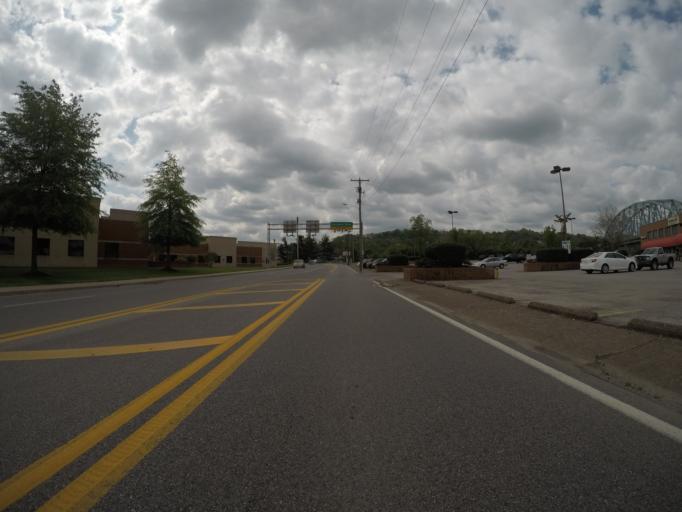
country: US
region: West Virginia
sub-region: Kanawha County
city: South Charleston
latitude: 38.3675
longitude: -81.6666
